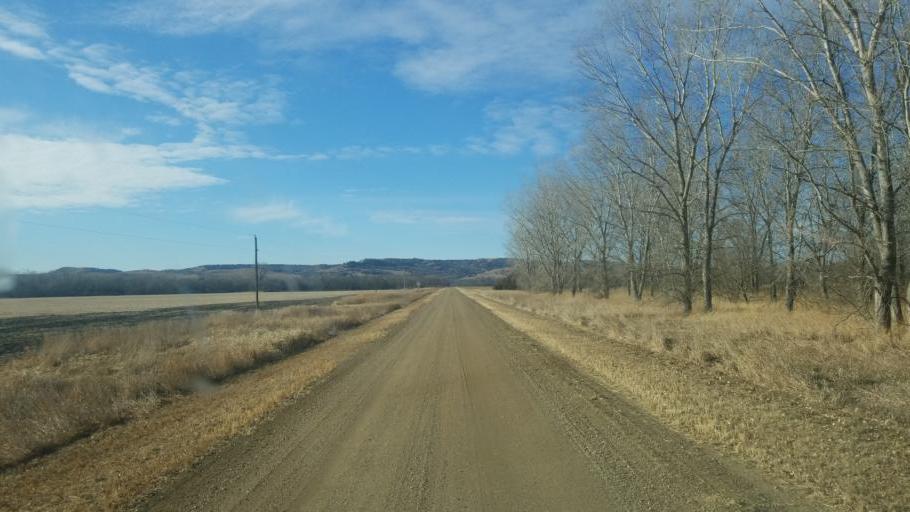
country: US
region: South Dakota
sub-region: Charles Mix County
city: Wagner
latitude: 42.9662
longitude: -98.4582
